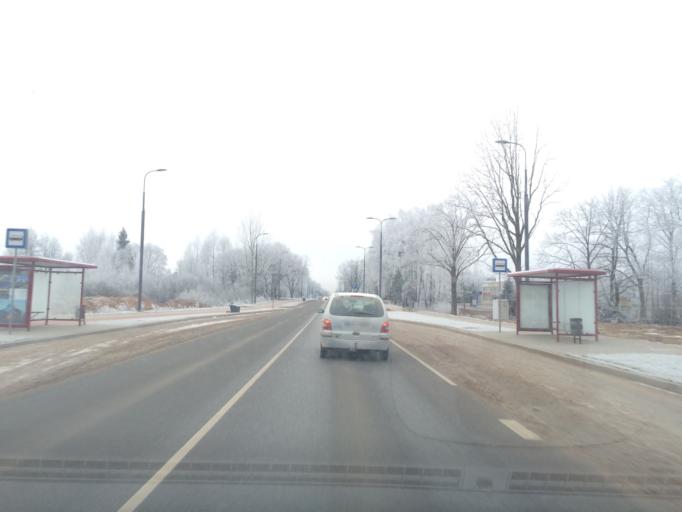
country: LV
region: Rezekne
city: Rezekne
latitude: 56.5362
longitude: 27.3489
